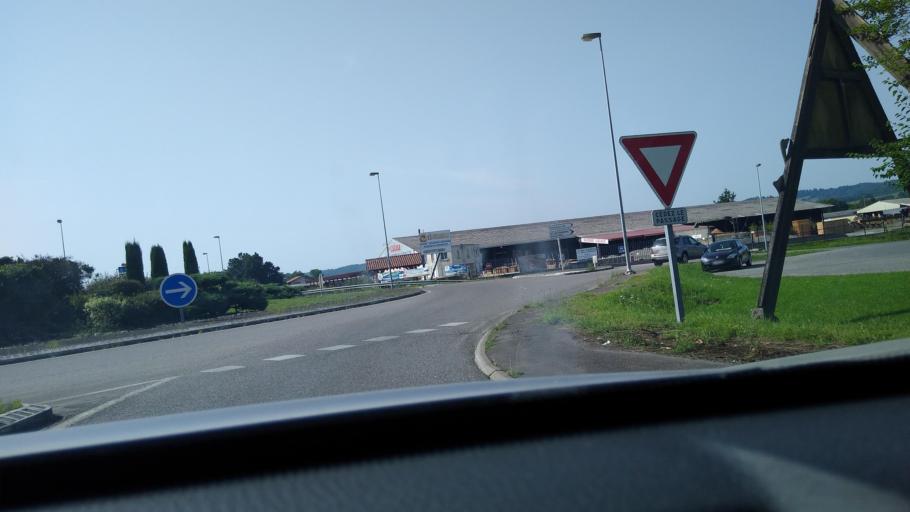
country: FR
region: Midi-Pyrenees
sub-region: Departement de l'Ariege
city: Saint-Lizier
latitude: 43.0205
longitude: 1.0998
